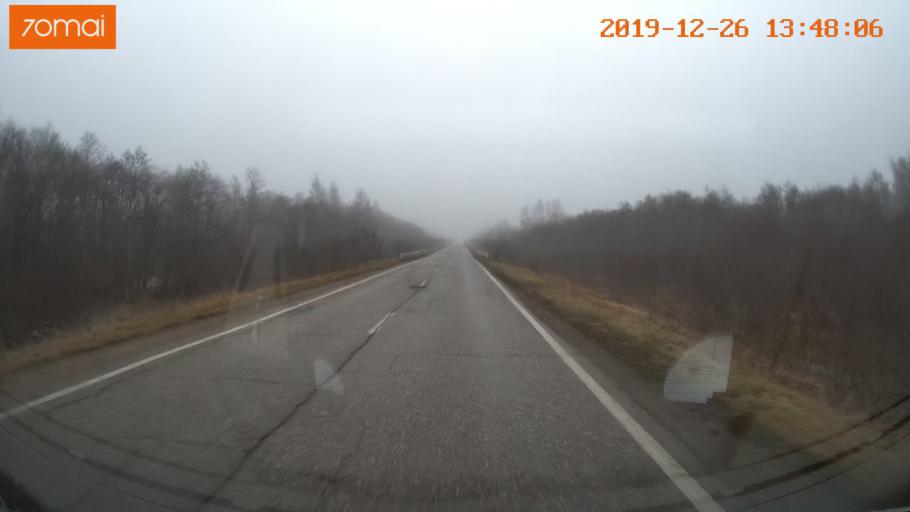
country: RU
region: Vologda
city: Sheksna
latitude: 58.6792
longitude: 38.5432
